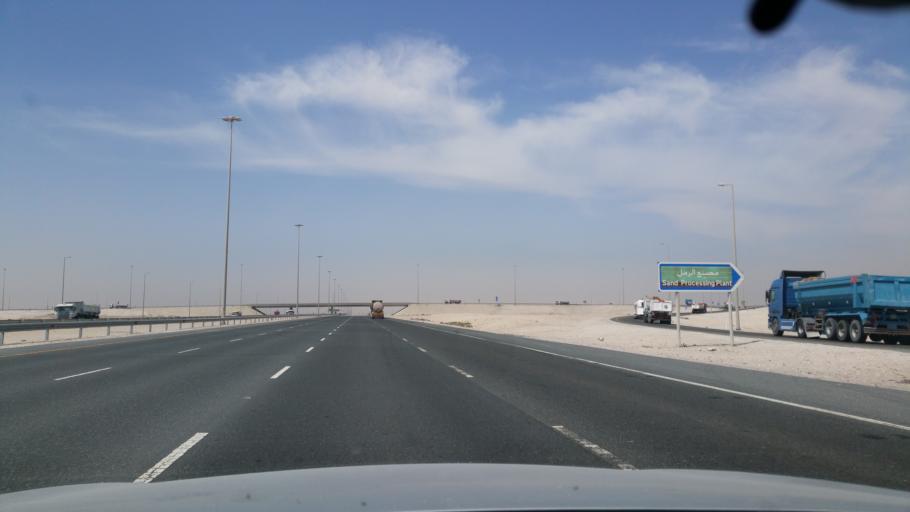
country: QA
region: Baladiyat ar Rayyan
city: Ash Shahaniyah
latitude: 25.1117
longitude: 51.1722
